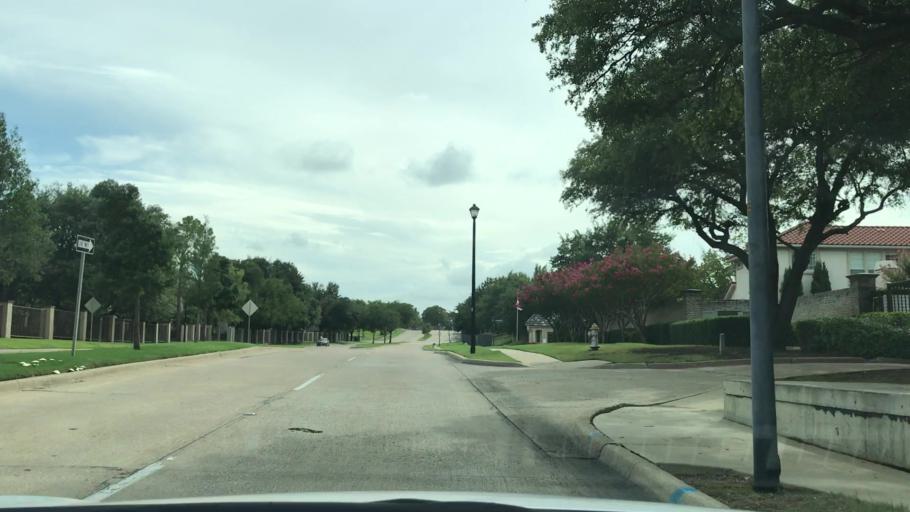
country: US
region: Texas
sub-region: Dallas County
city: Irving
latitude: 32.8612
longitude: -96.9528
